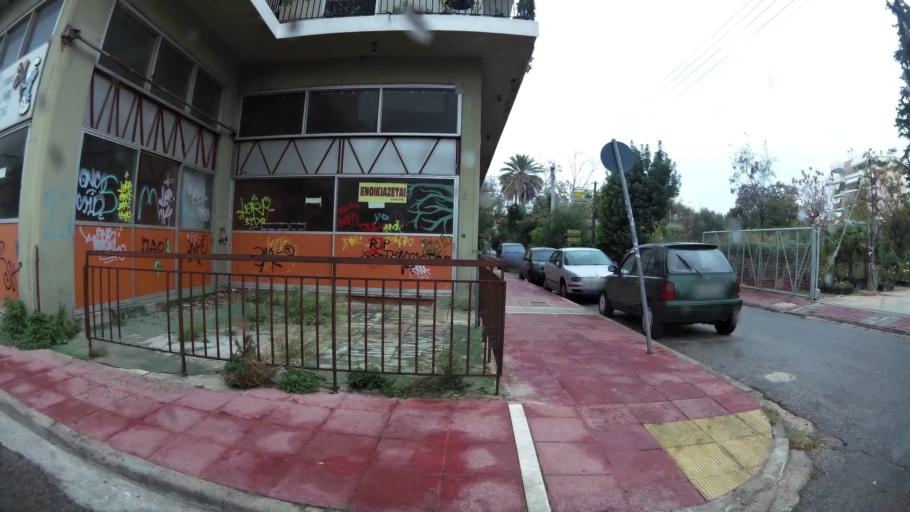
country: GR
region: Attica
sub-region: Nomarchia Athinas
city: Agioi Anargyroi
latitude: 38.0183
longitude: 23.7170
